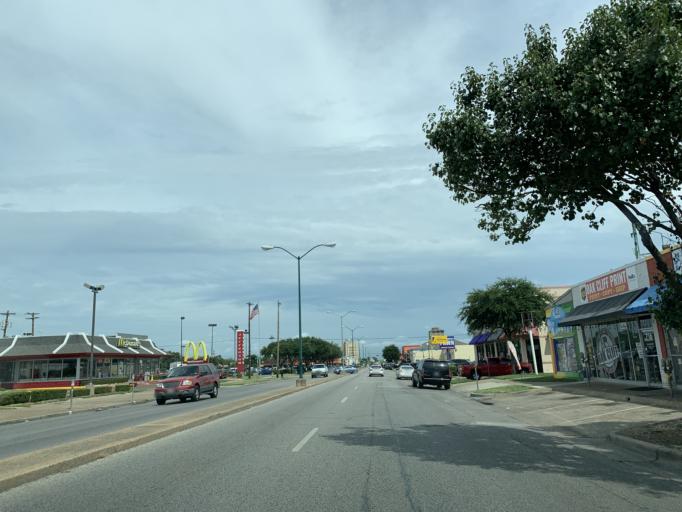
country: US
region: Texas
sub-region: Dallas County
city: Dallas
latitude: 32.7431
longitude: -96.8350
